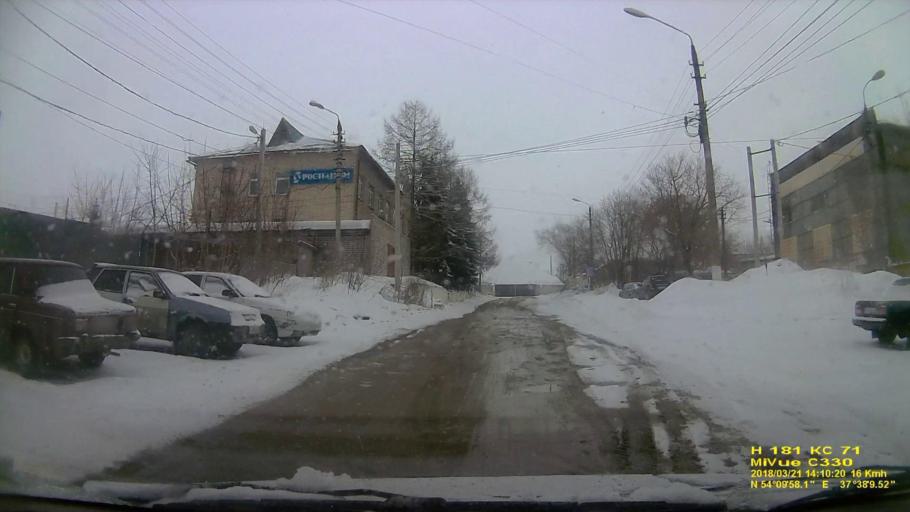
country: RU
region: Tula
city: Tula
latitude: 54.1661
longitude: 37.6360
